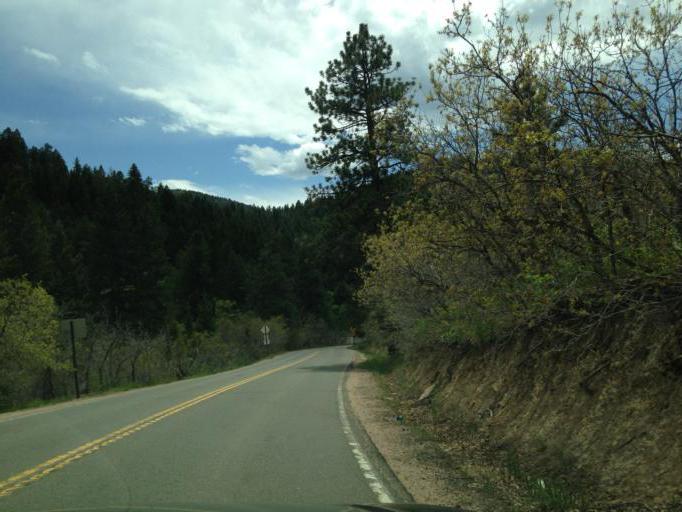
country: US
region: Colorado
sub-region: Jefferson County
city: Ken Caryl
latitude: 39.5063
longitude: -105.1869
